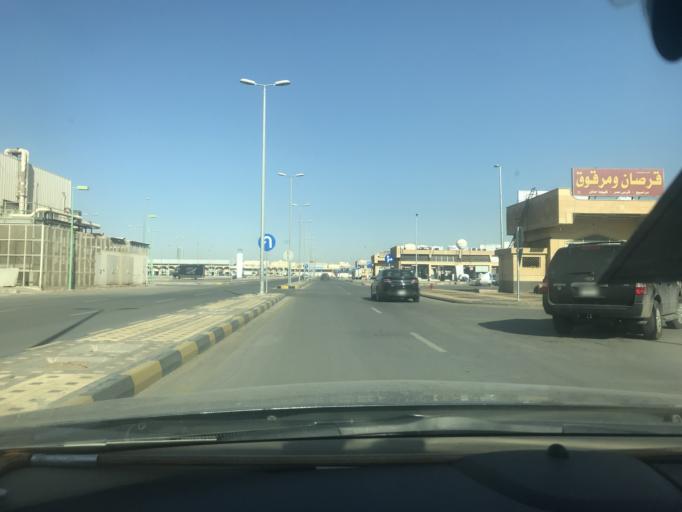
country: SA
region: Ar Riyad
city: Riyadh
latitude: 24.7536
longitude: 46.6665
